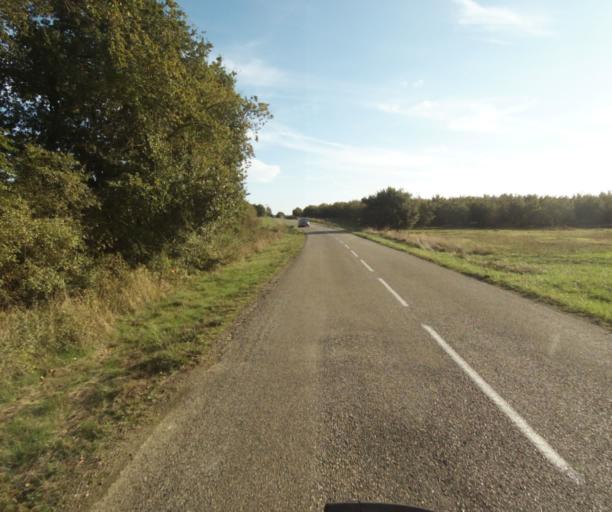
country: FR
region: Midi-Pyrenees
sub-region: Departement du Tarn-et-Garonne
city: Finhan
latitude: 43.9030
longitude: 1.1242
